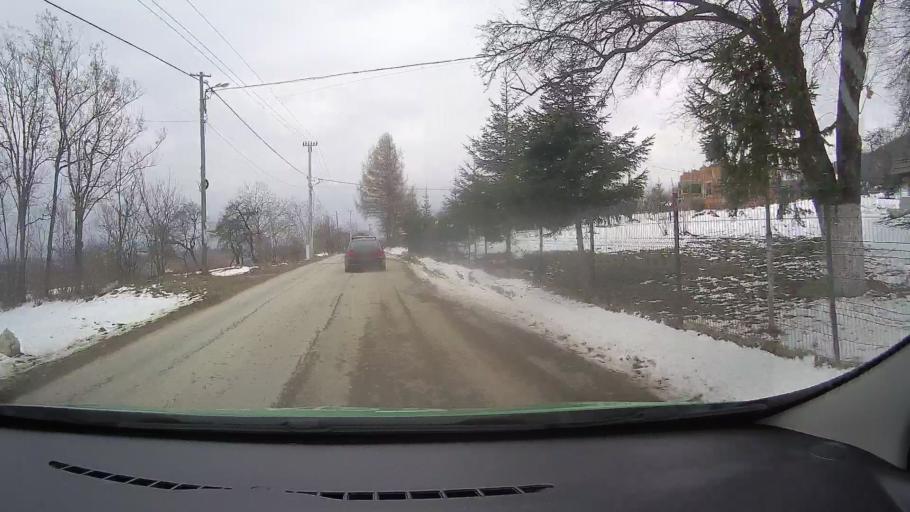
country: RO
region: Brasov
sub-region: Comuna Bran
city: Bran
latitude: 45.5375
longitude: 25.3369
